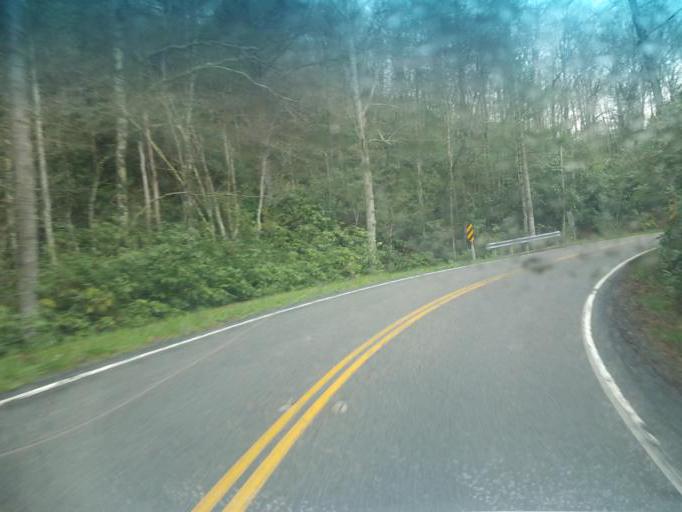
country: US
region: Virginia
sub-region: Smyth County
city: Chilhowie
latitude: 36.6515
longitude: -81.7027
